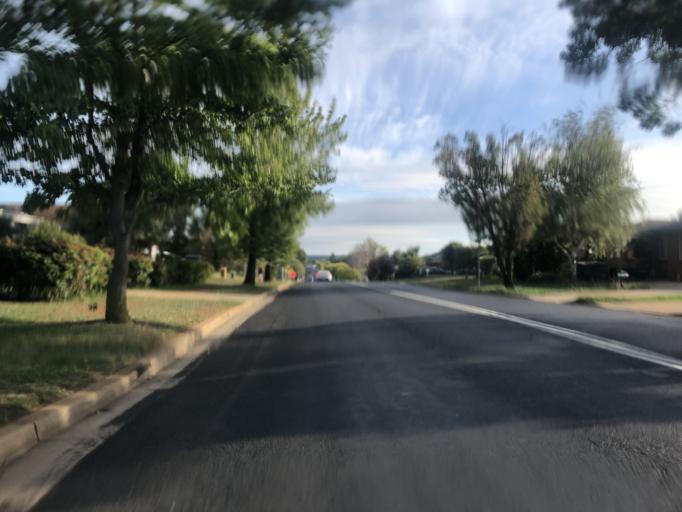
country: AU
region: New South Wales
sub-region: Orange Municipality
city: Orange
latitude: -33.3038
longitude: 149.0947
